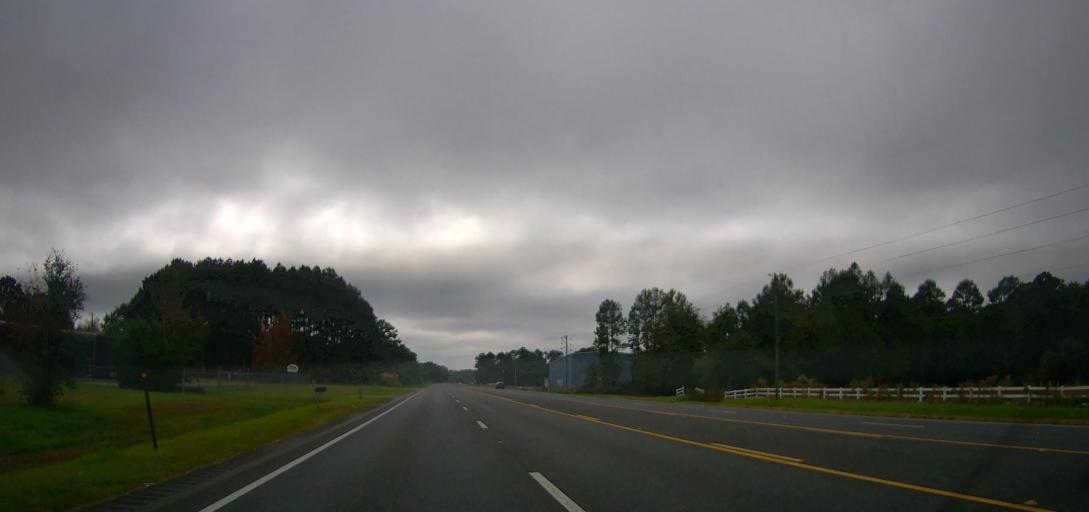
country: US
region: Georgia
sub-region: Thomas County
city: Thomasville
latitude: 30.9898
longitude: -83.8765
